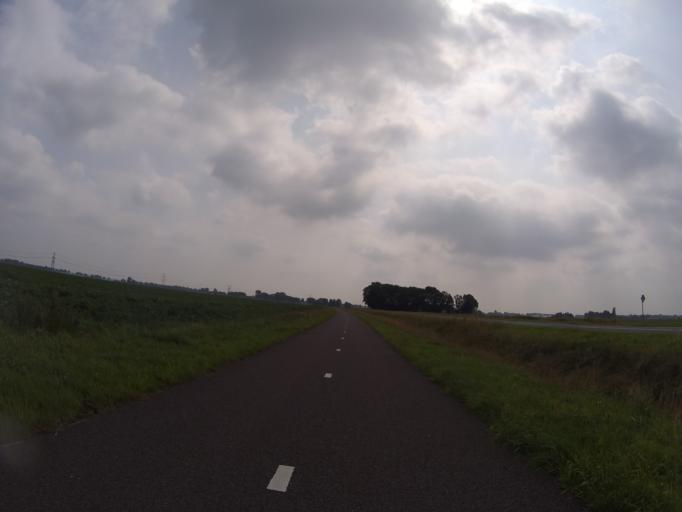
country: NL
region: Drenthe
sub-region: Gemeente Emmen
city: Emmer-Compascuum
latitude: 52.8778
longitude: 6.9942
